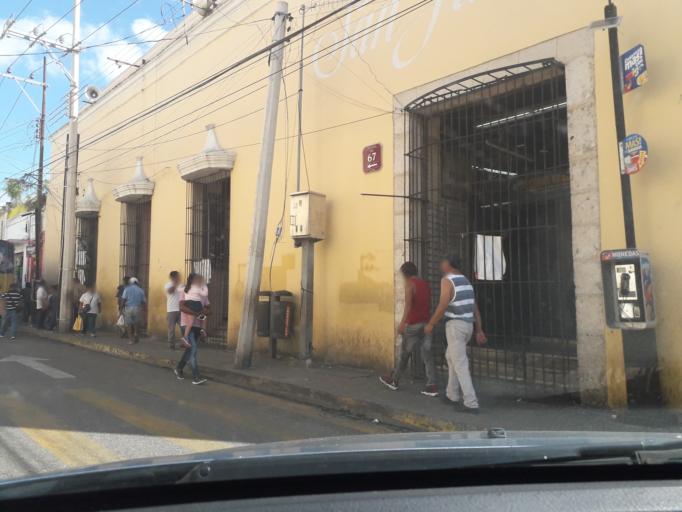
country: MX
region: Yucatan
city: Merida
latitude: 20.9636
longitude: -89.6250
